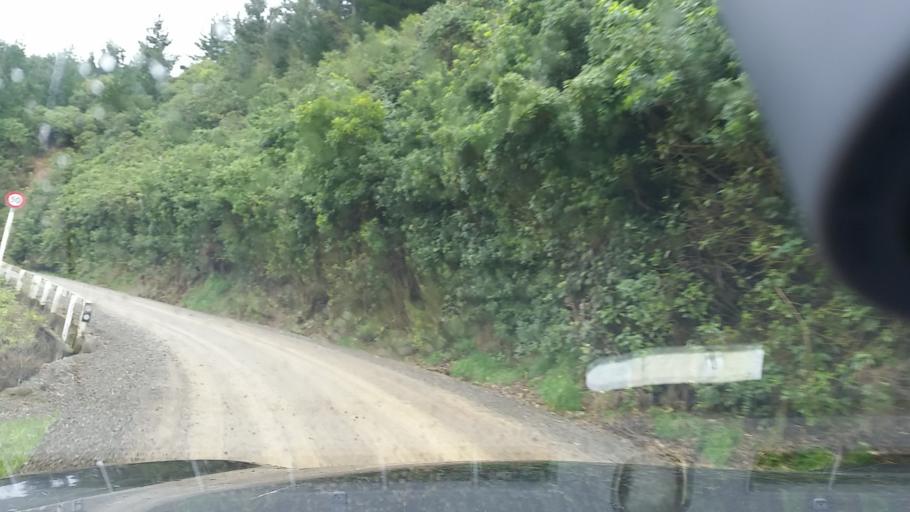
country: NZ
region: Marlborough
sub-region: Marlborough District
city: Picton
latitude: -41.3633
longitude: 174.0718
